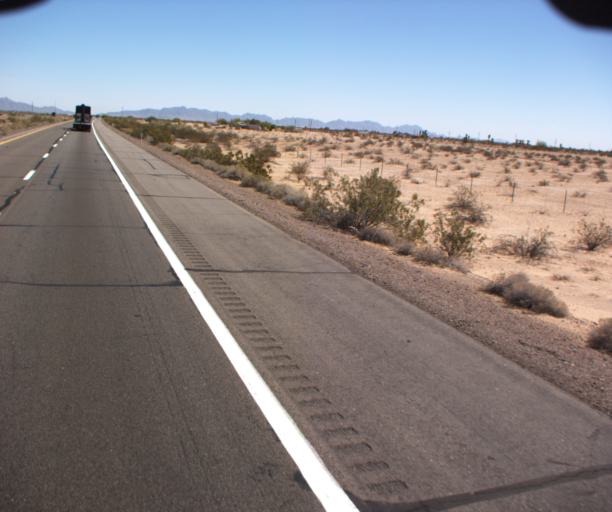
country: US
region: Arizona
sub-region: Yuma County
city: Wellton
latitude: 32.6868
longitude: -113.9958
